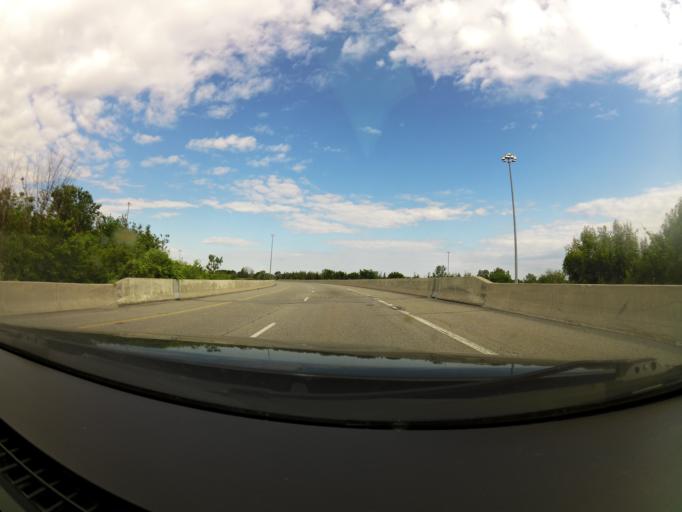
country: CA
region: Ontario
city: Bells Corners
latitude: 45.3420
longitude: -75.8168
